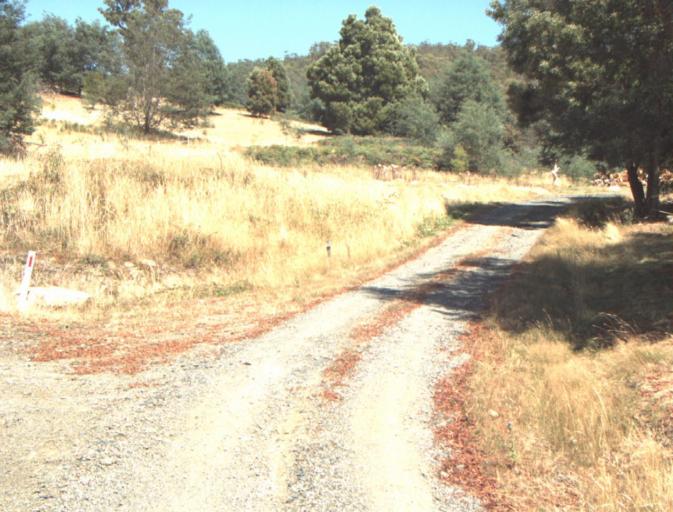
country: AU
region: Tasmania
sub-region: Launceston
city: Mayfield
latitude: -41.2487
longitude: 147.1209
